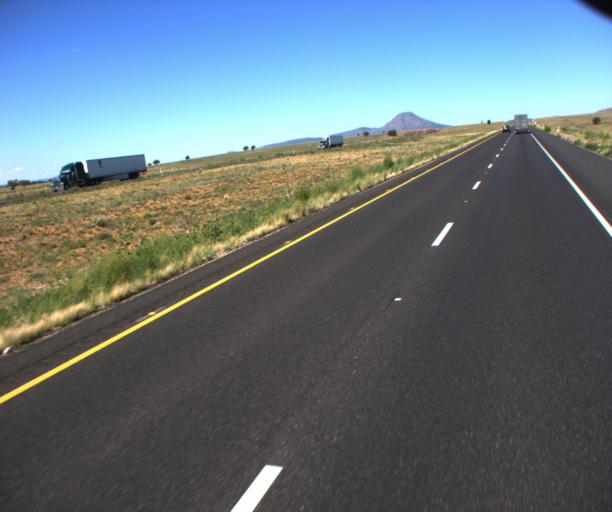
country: US
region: Arizona
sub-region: Yavapai County
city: Paulden
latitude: 35.2333
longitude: -112.6137
